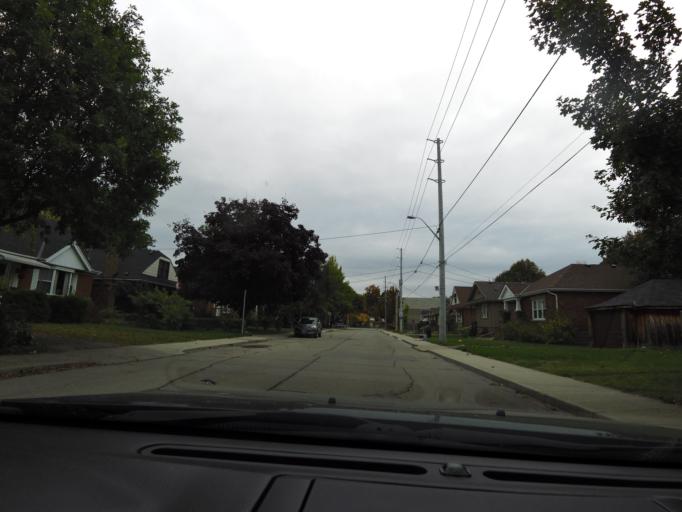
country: CA
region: Ontario
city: Hamilton
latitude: 43.2567
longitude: -79.9153
